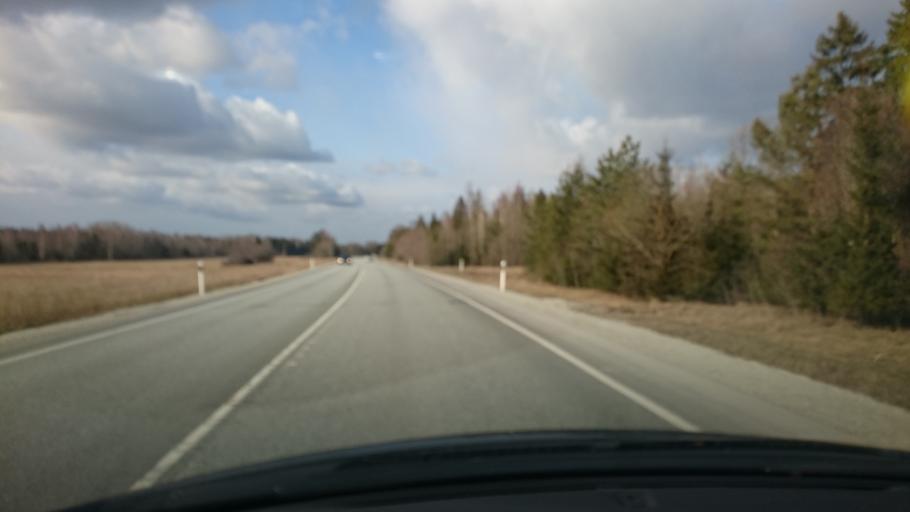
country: EE
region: Harju
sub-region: Nissi vald
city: Riisipere
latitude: 59.1348
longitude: 24.3282
